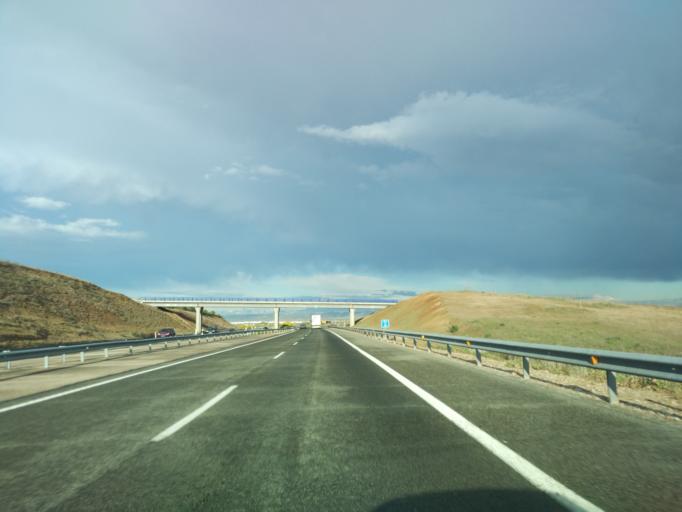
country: ES
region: Madrid
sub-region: Provincia de Madrid
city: Ajalvir
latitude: 40.5059
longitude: -3.4529
